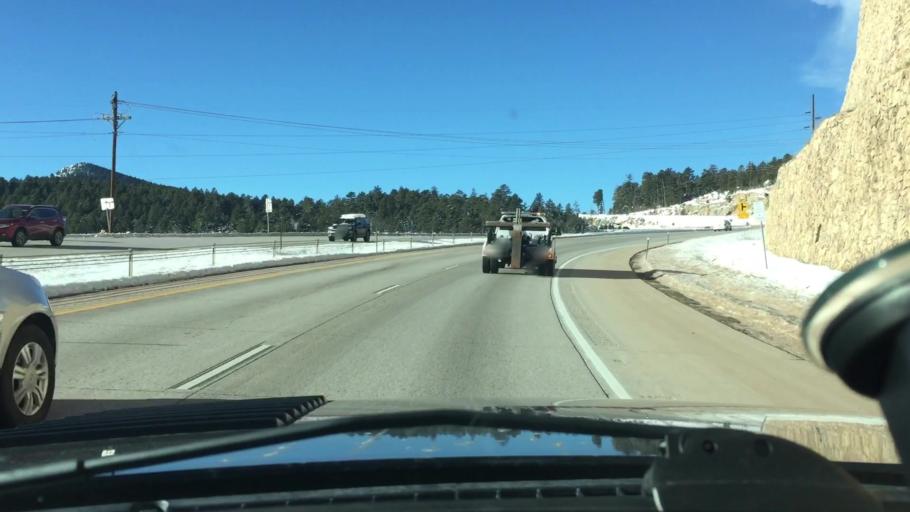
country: US
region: Colorado
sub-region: Jefferson County
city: Indian Hills
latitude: 39.5536
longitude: -105.2419
